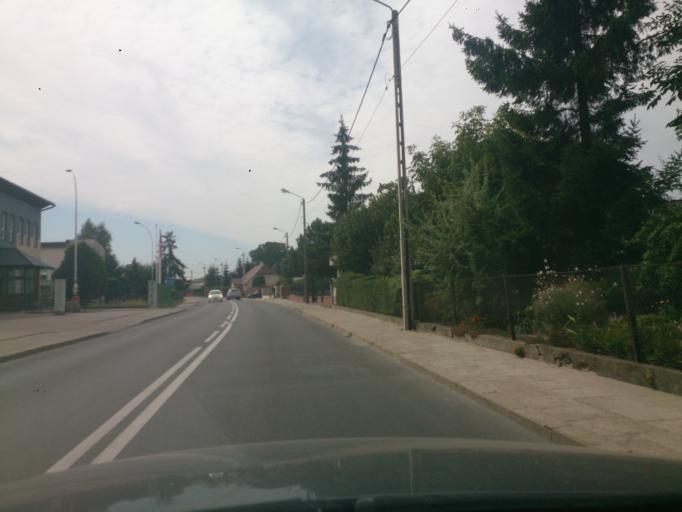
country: PL
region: Subcarpathian Voivodeship
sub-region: Powiat kolbuszowski
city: Kolbuszowa
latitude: 50.2391
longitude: 21.7718
